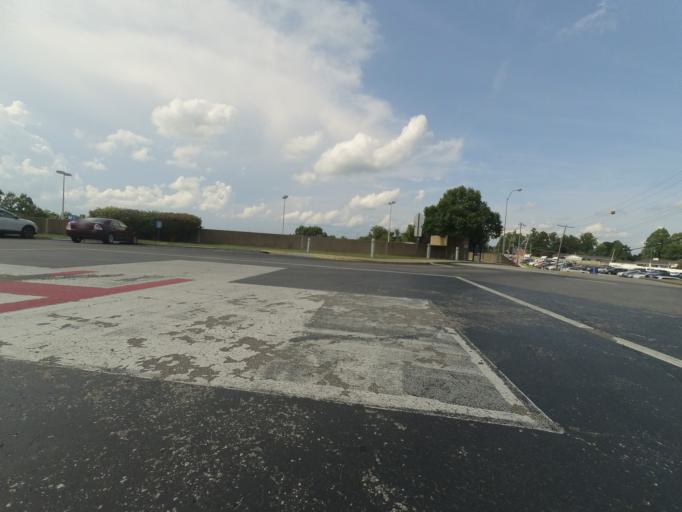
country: US
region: Ohio
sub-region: Lawrence County
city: Burlington
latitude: 38.3773
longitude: -82.5158
